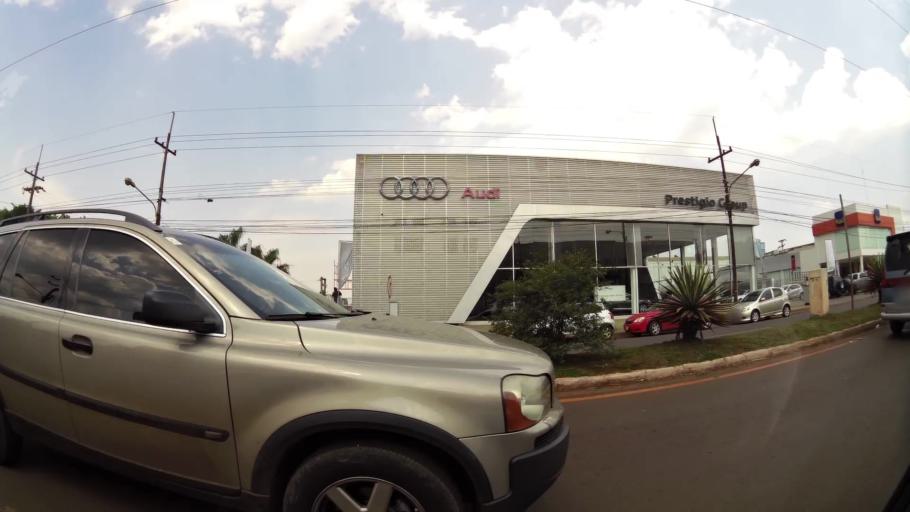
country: PY
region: Alto Parana
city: Ciudad del Este
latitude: -25.4970
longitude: -54.6345
